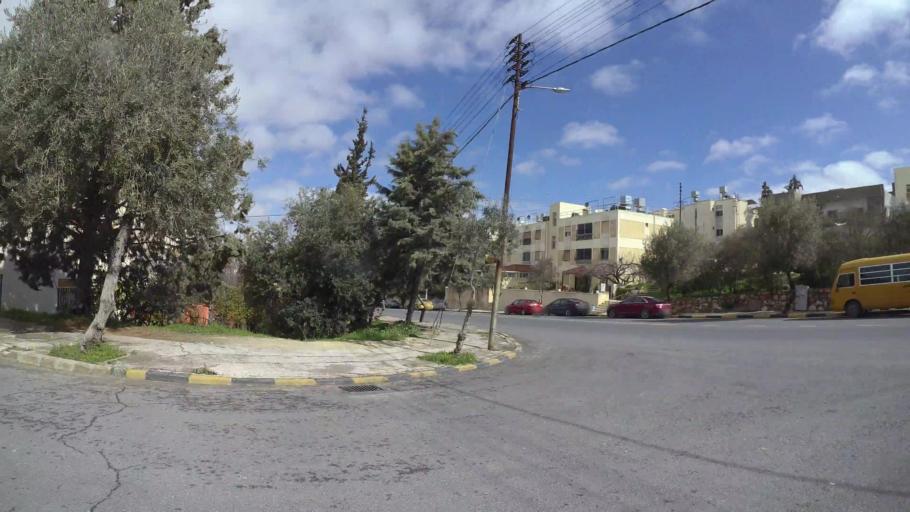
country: JO
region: Amman
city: Al Jubayhah
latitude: 32.0563
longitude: 35.8846
